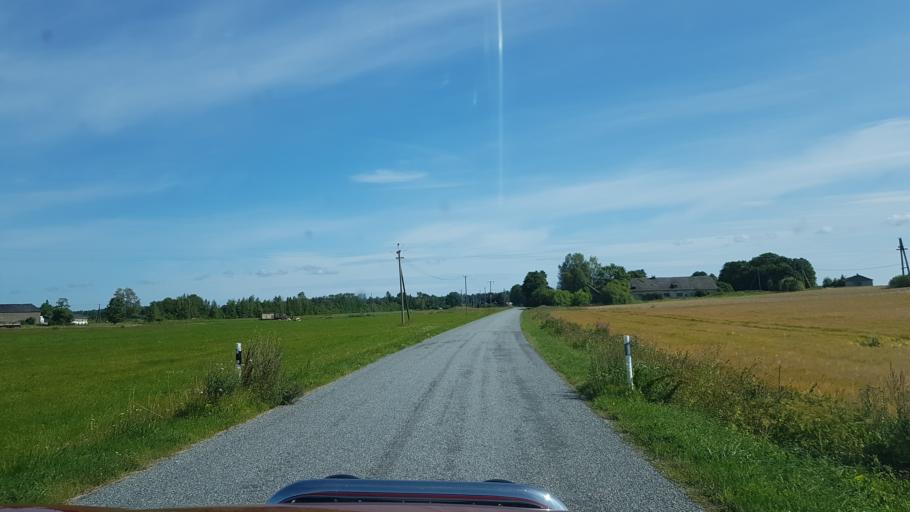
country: EE
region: Jaervamaa
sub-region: Jaerva-Jaani vald
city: Jarva-Jaani
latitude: 59.1109
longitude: 25.7798
